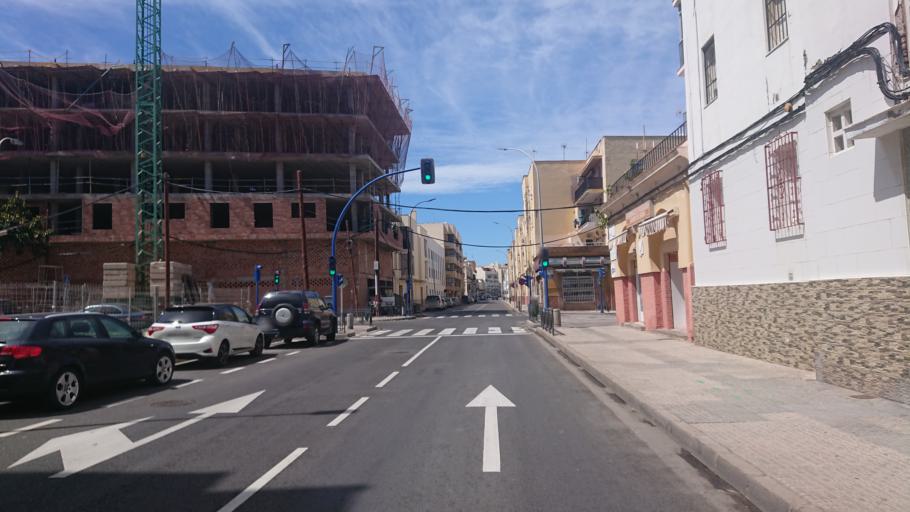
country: ES
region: Melilla
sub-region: Melilla
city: Melilla
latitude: 35.2819
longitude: -2.9407
